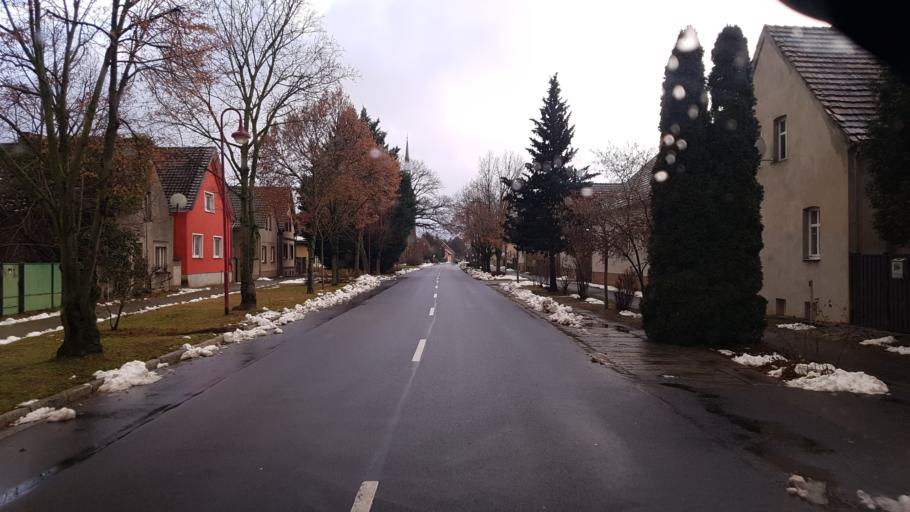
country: DE
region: Brandenburg
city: Heinersbruck
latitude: 51.8193
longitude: 14.5076
